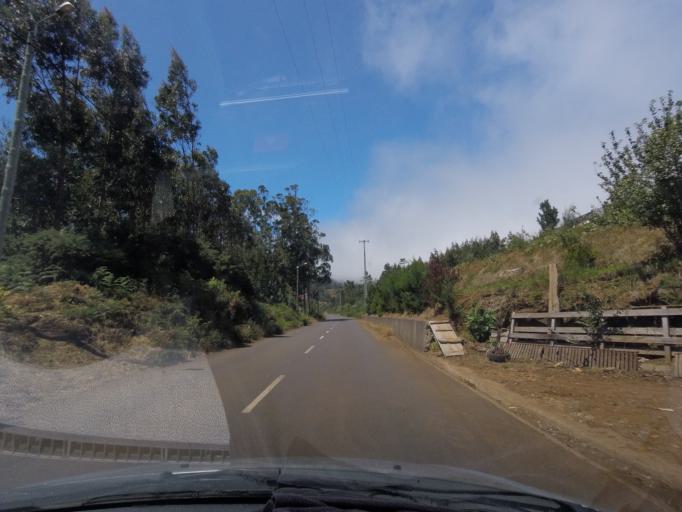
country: PT
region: Madeira
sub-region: Santa Cruz
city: Camacha
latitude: 32.6918
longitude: -16.8339
